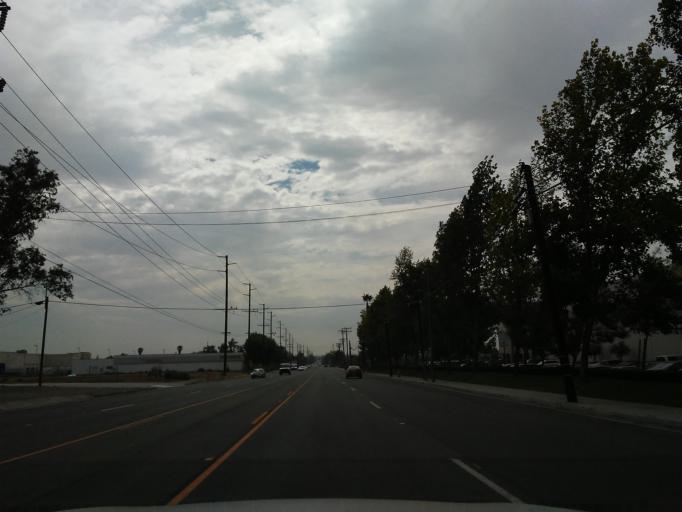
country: US
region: California
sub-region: San Bernardino County
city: San Bernardino
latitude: 34.0922
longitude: -117.2740
